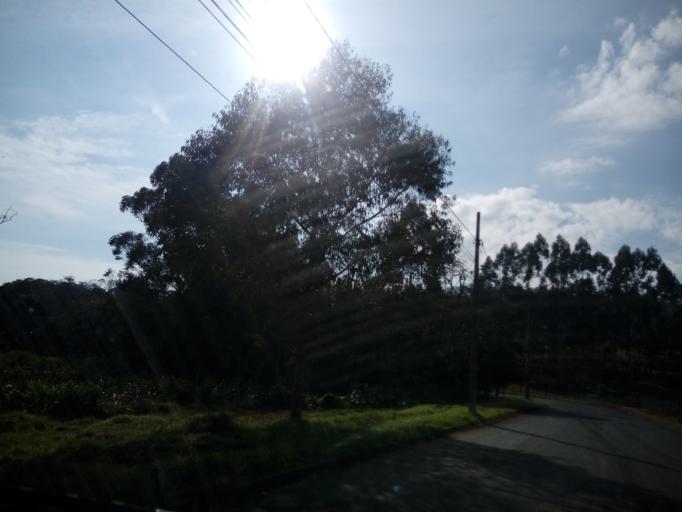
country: BR
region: Santa Catarina
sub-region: Chapeco
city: Chapeco
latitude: -27.1071
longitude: -52.5905
